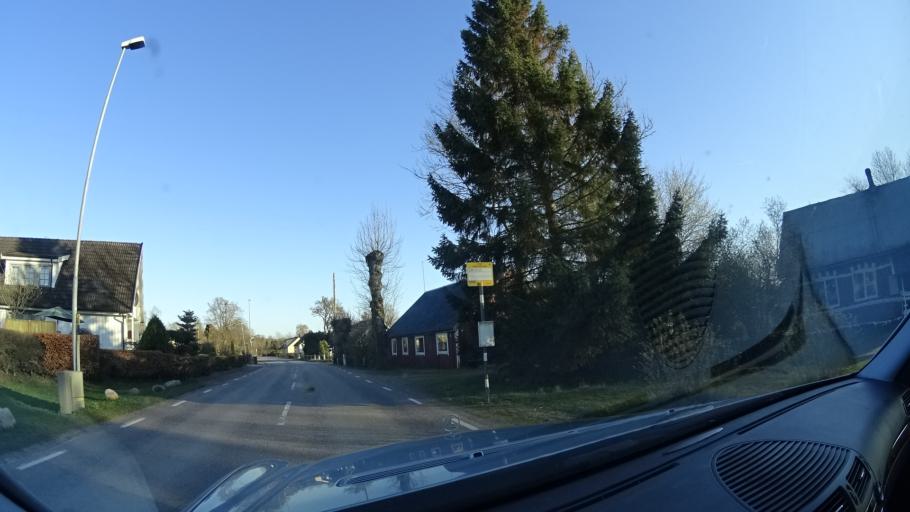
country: SE
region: Skane
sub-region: Bjuvs Kommun
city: Billesholm
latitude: 56.0478
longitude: 13.0018
